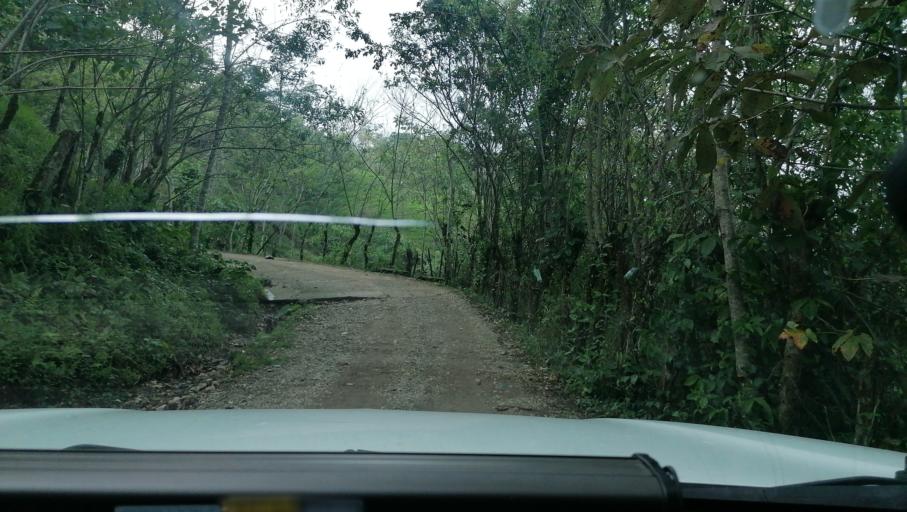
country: MX
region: Chiapas
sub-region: Tapilula
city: San Francisco Jacona
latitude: 17.3313
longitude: -93.1026
